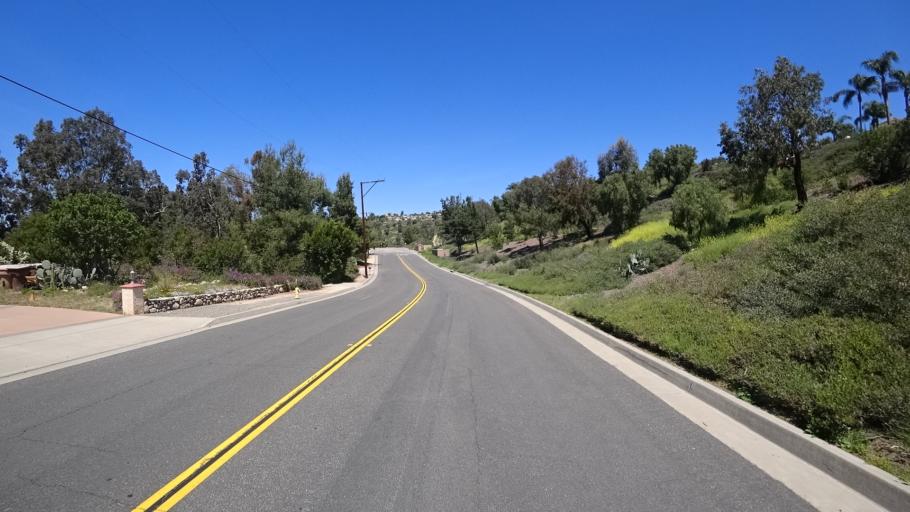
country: US
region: California
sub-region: Orange County
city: Villa Park
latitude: 33.8273
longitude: -117.7943
